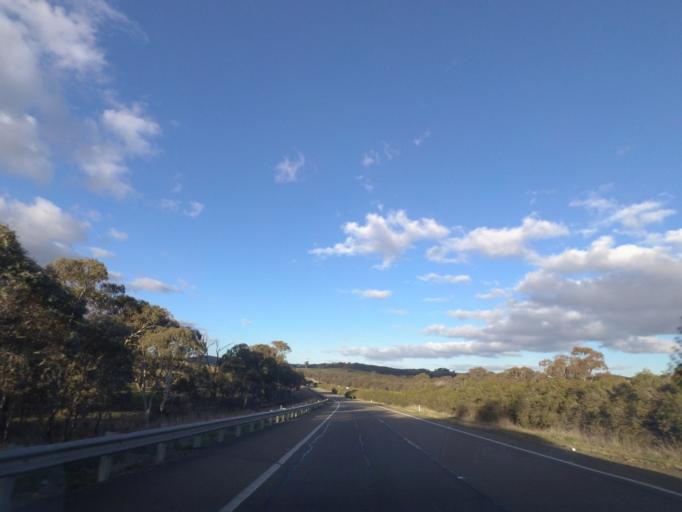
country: AU
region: New South Wales
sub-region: Yass Valley
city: Yass
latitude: -34.8134
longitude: 148.6070
